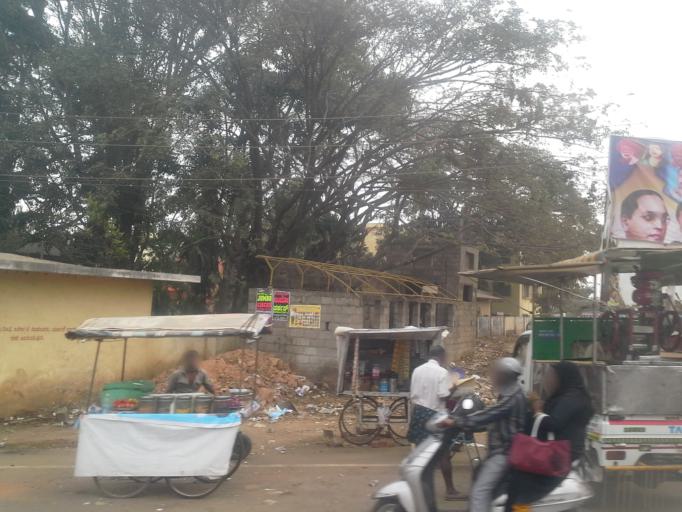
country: IN
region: Karnataka
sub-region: Bangalore Urban
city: Bangalore
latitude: 13.0082
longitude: 77.6929
